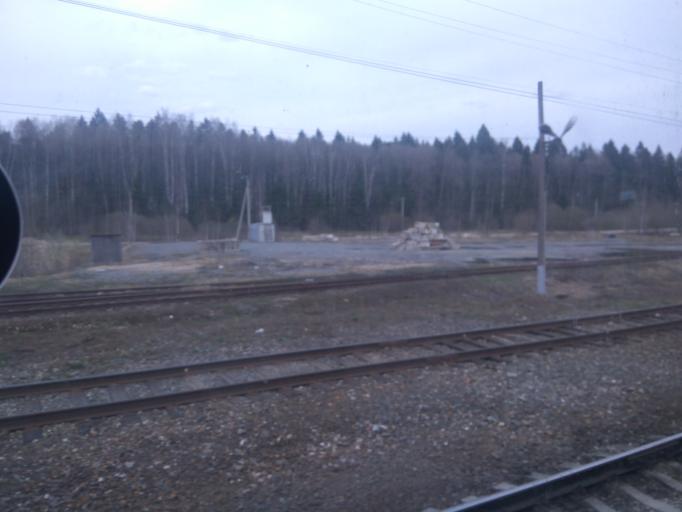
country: RU
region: Moskovskaya
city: Svatkovo
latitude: 56.3901
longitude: 38.3182
